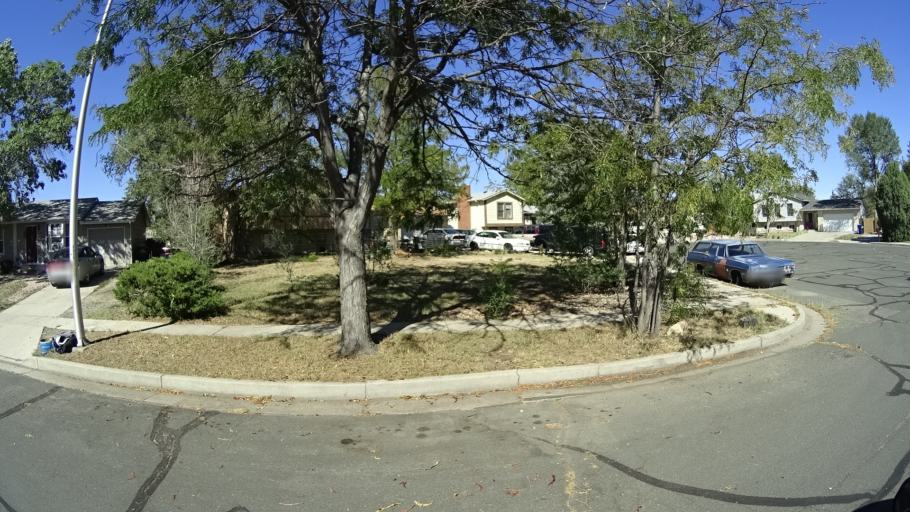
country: US
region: Colorado
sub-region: El Paso County
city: Stratmoor
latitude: 38.7931
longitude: -104.7432
